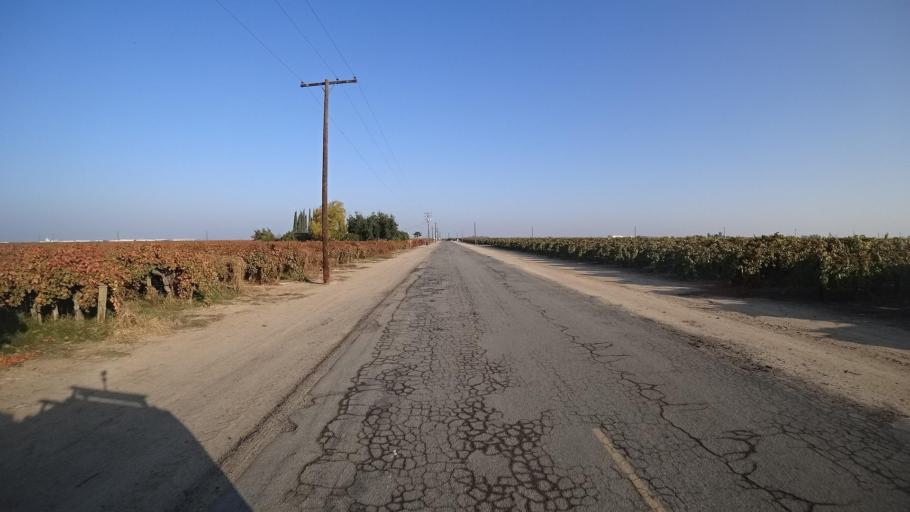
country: US
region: California
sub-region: Tulare County
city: Richgrove
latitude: 35.7881
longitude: -119.1341
